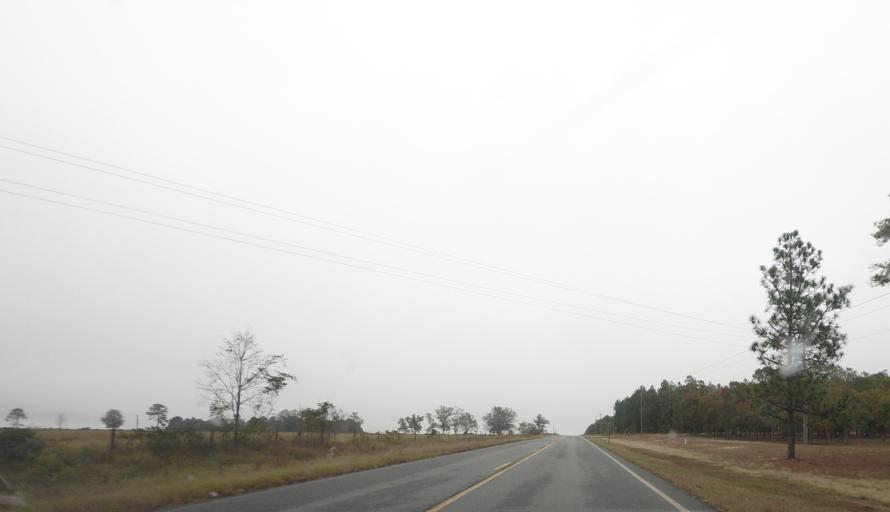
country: US
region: Georgia
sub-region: Marion County
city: Buena Vista
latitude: 32.4070
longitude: -84.4073
